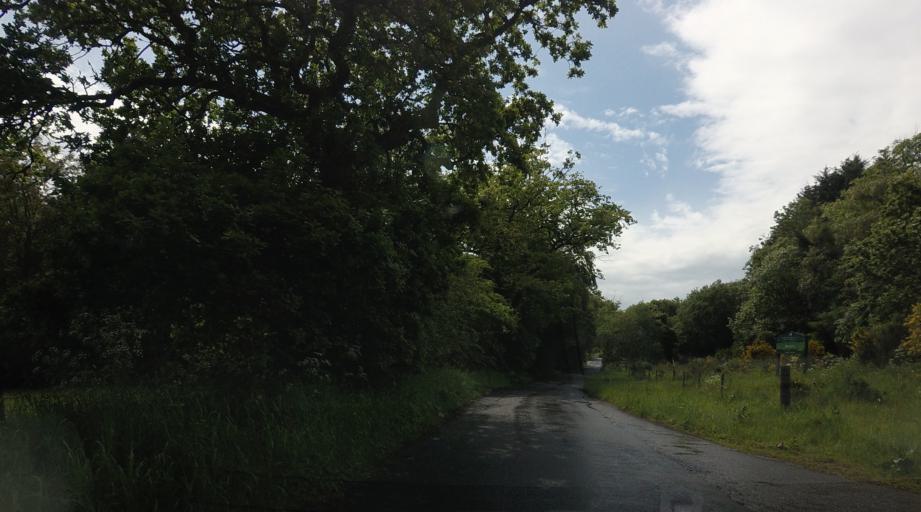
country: GB
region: Scotland
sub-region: Fife
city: Ballingry
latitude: 56.1620
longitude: -3.3429
